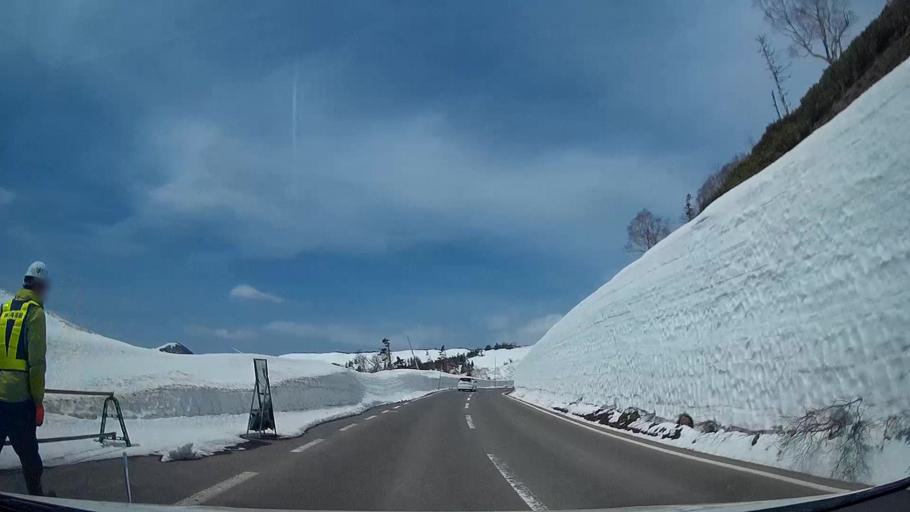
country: JP
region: Akita
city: Hanawa
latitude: 39.9515
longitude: 140.8665
